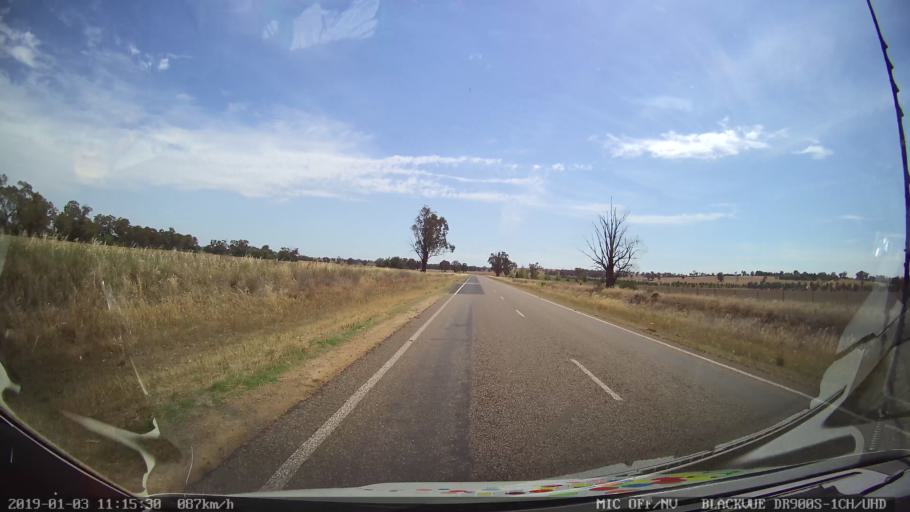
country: AU
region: New South Wales
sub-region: Young
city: Young
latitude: -34.1633
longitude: 148.2651
